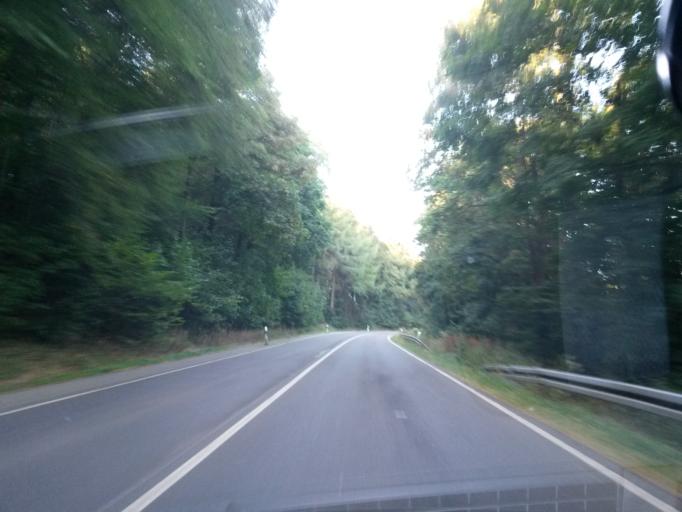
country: DE
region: North Rhine-Westphalia
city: Kierspe
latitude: 51.1192
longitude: 7.5901
